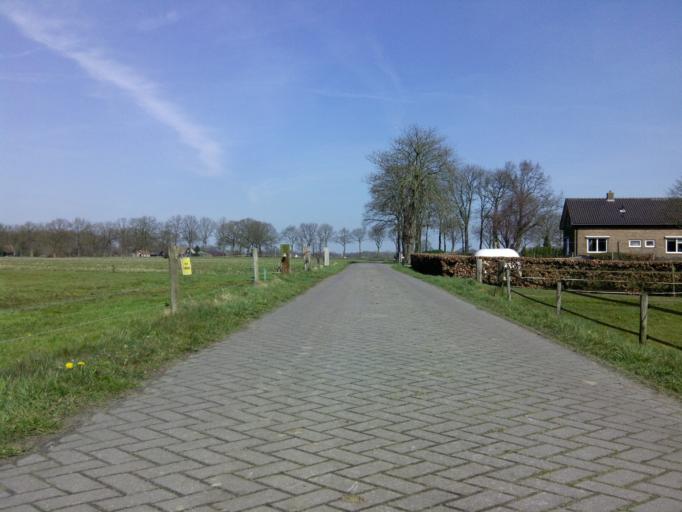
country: NL
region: Gelderland
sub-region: Gemeente Putten
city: Putten
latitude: 52.2238
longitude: 5.5794
